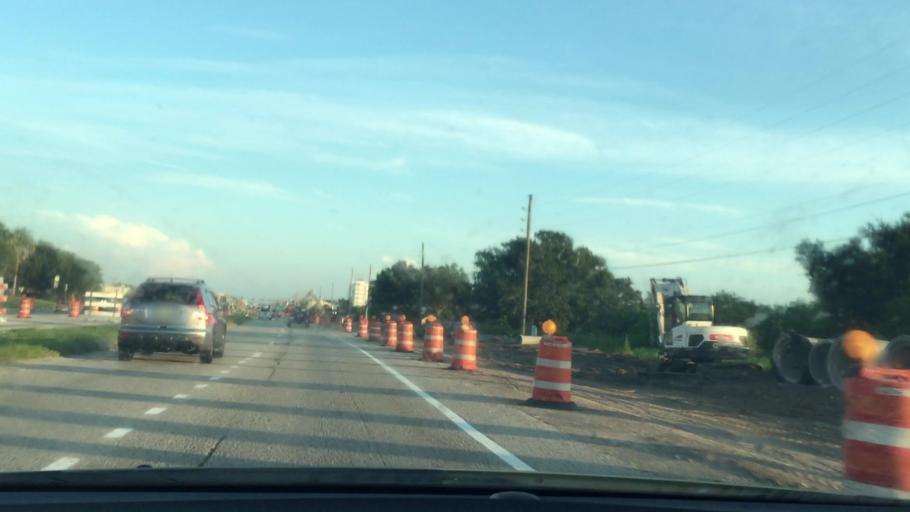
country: US
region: Florida
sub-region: Osceola County
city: Buenaventura Lakes
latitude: 28.2790
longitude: -81.3433
